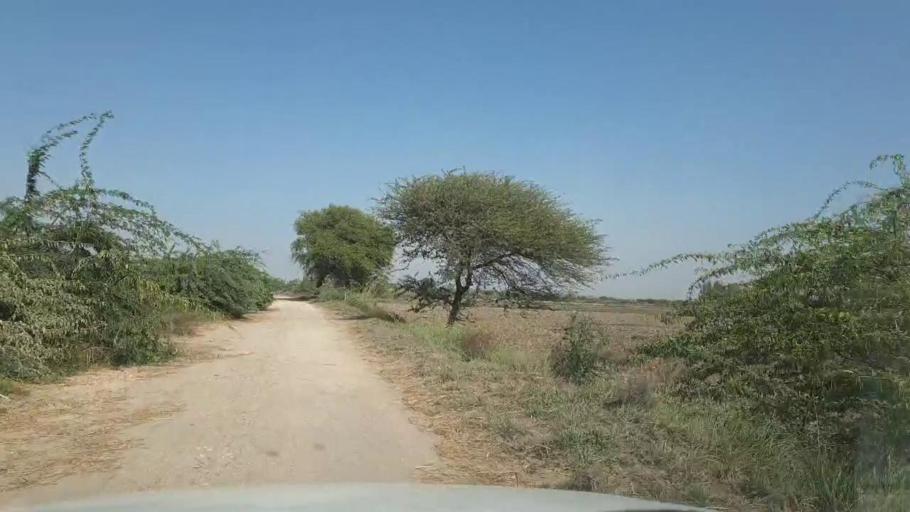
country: PK
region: Sindh
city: Mirpur Sakro
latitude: 24.4030
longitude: 67.7482
